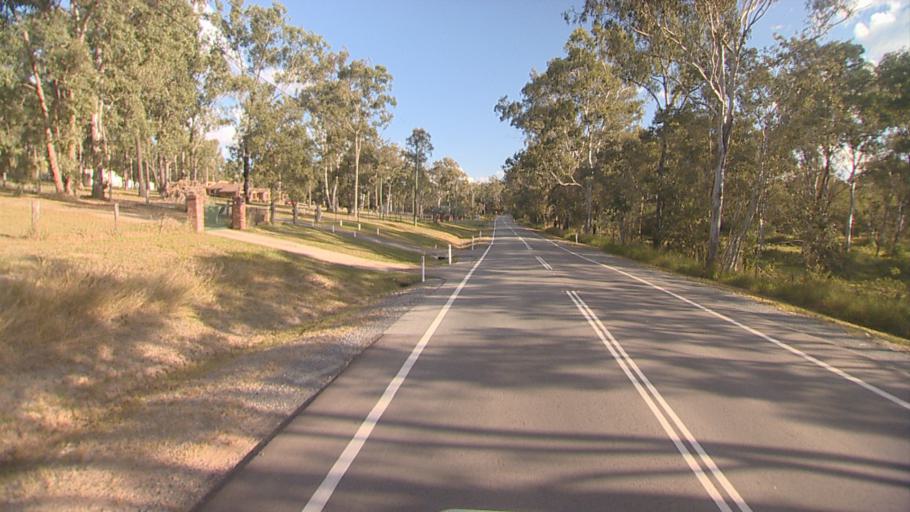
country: AU
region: Queensland
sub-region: Ipswich
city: Springfield Lakes
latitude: -27.7251
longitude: 152.9574
